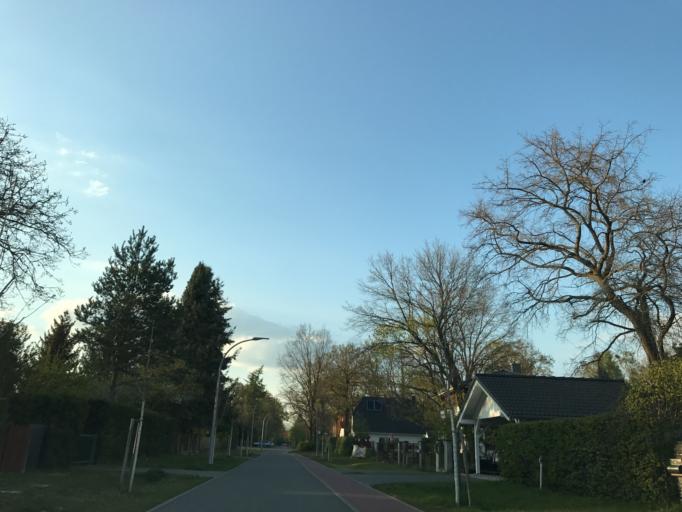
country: DE
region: Brandenburg
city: Dallgow-Doeberitz
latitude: 52.5562
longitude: 13.0571
